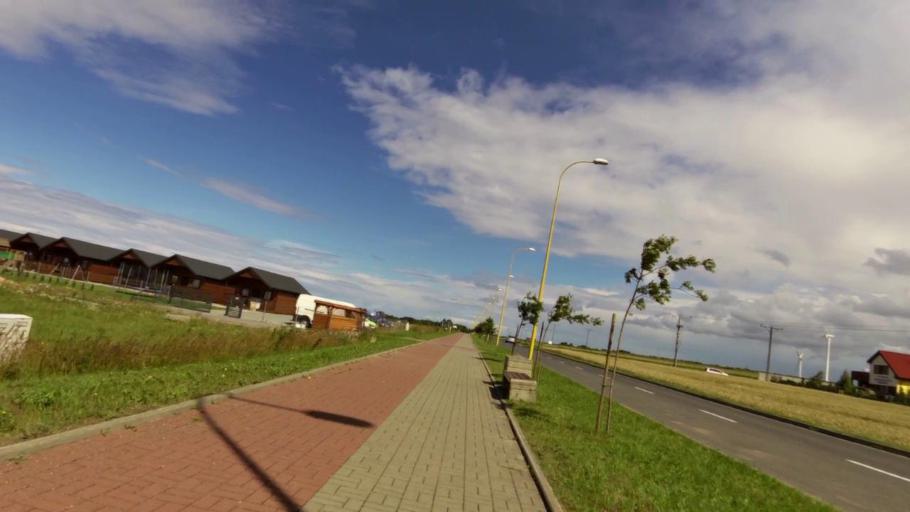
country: PL
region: West Pomeranian Voivodeship
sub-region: Powiat slawienski
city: Darlowo
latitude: 54.4369
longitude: 16.4093
